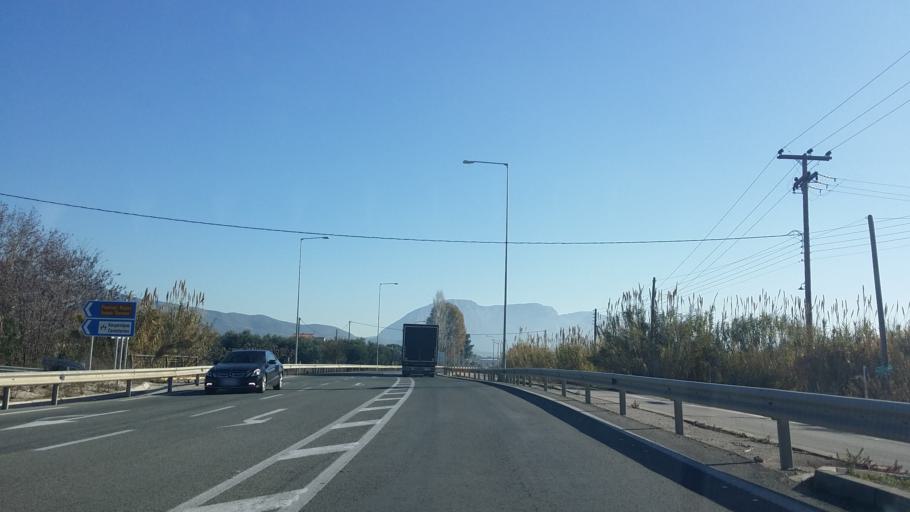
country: GR
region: West Greece
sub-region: Nomos Aitolias kai Akarnanias
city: Mesolongi
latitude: 38.3805
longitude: 21.4606
